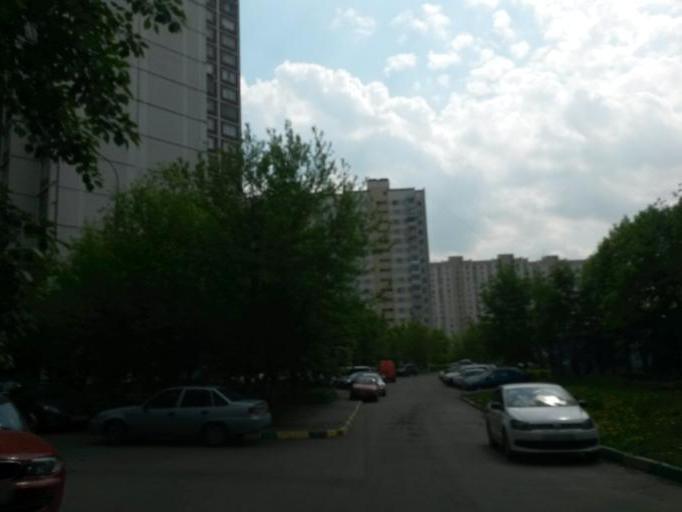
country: RU
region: Moscow
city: Mar'ino
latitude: 55.6511
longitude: 37.7402
